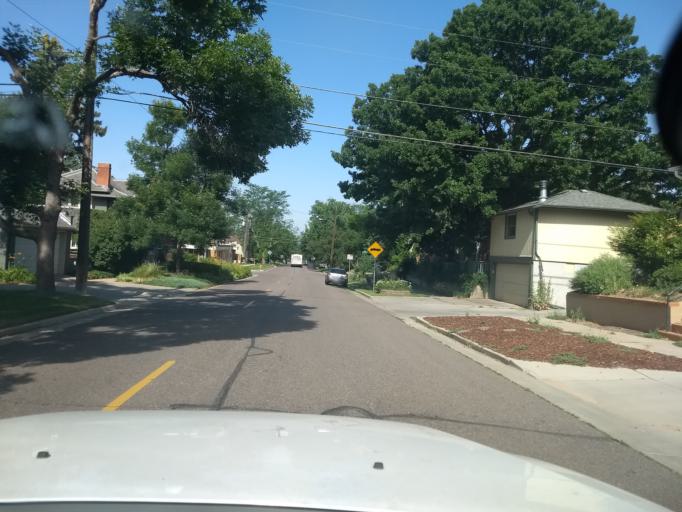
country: US
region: Colorado
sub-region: Arapahoe County
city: Englewood
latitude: 39.6876
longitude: -104.9750
